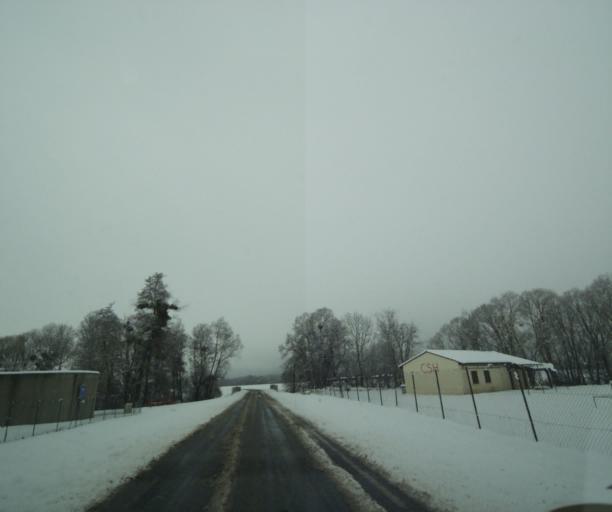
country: FR
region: Champagne-Ardenne
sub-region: Departement de la Haute-Marne
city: Saint-Dizier
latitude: 48.5773
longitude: 4.8926
